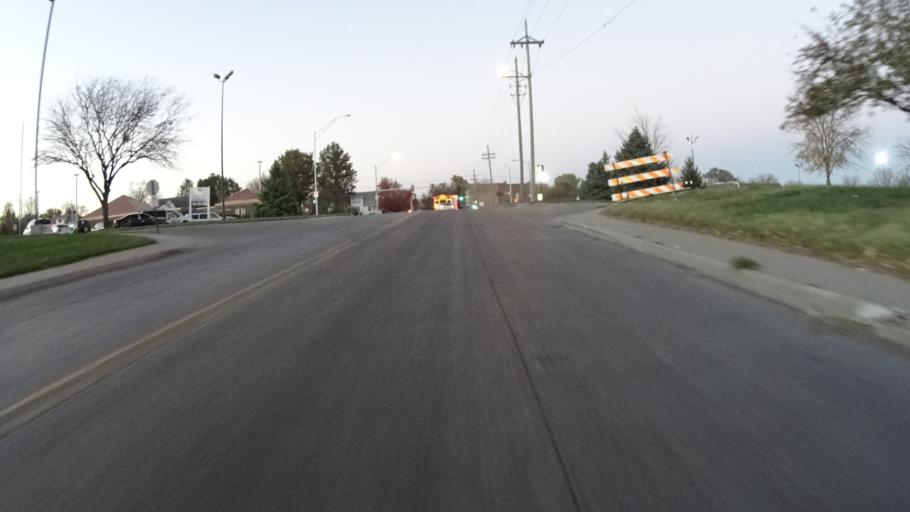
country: US
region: Nebraska
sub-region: Douglas County
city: Omaha
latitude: 41.2110
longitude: -95.9627
